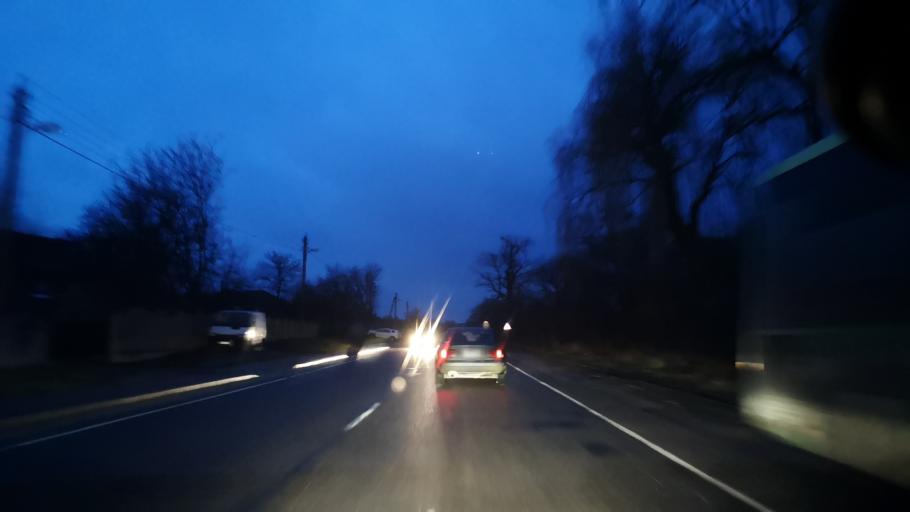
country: MD
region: Orhei
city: Orhei
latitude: 47.4263
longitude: 28.8034
